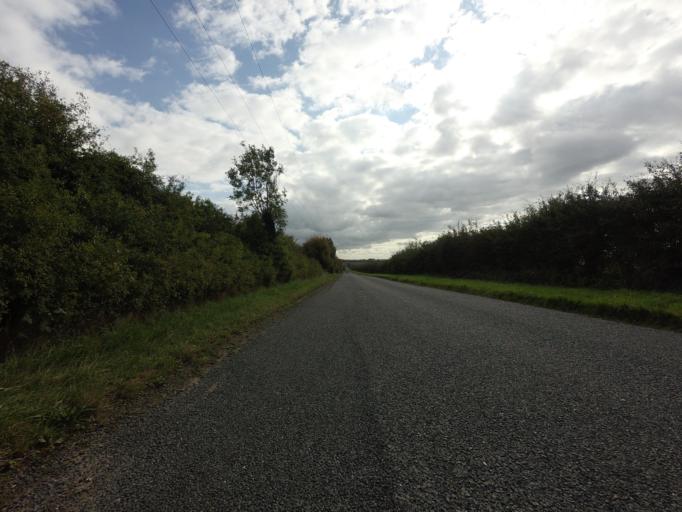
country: GB
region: England
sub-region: Norfolk
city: Heacham
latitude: 52.9160
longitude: 0.5426
